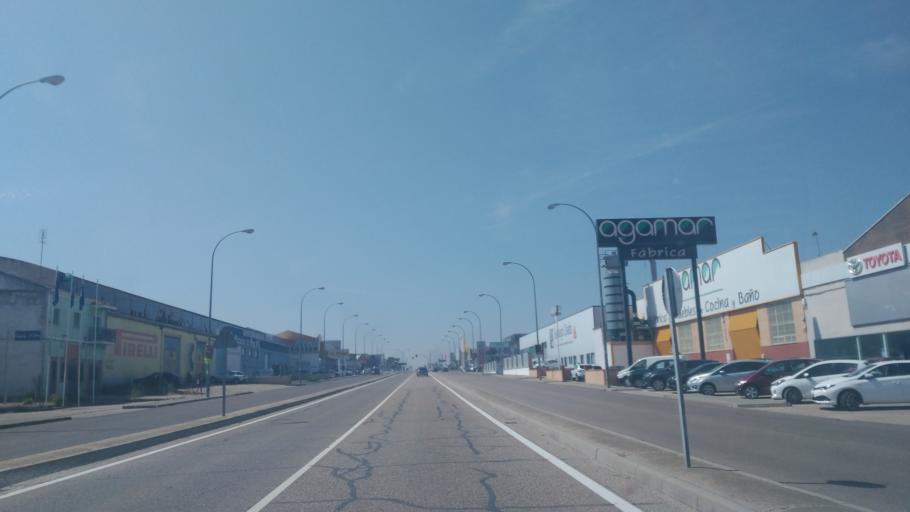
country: ES
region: Castille and Leon
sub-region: Provincia de Salamanca
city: Villares de la Reina
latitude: 40.9949
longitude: -5.6359
